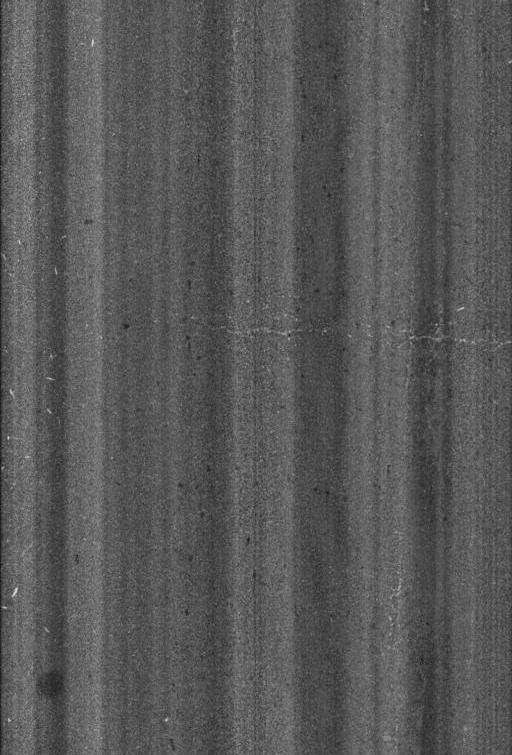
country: US
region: Washington, D.C.
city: Washington, D.C.
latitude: 38.8739
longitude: -77.0144
